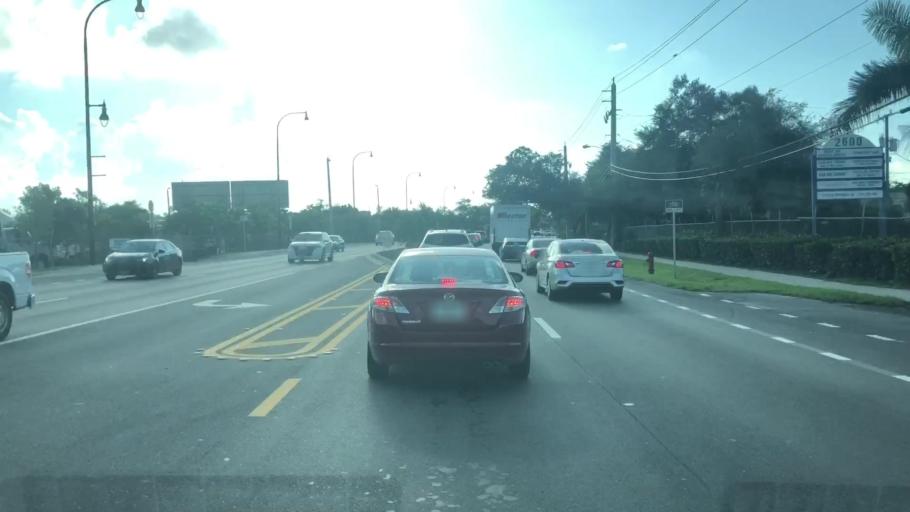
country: US
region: Florida
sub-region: Broward County
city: Coconut Creek
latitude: 26.2453
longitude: -80.1575
